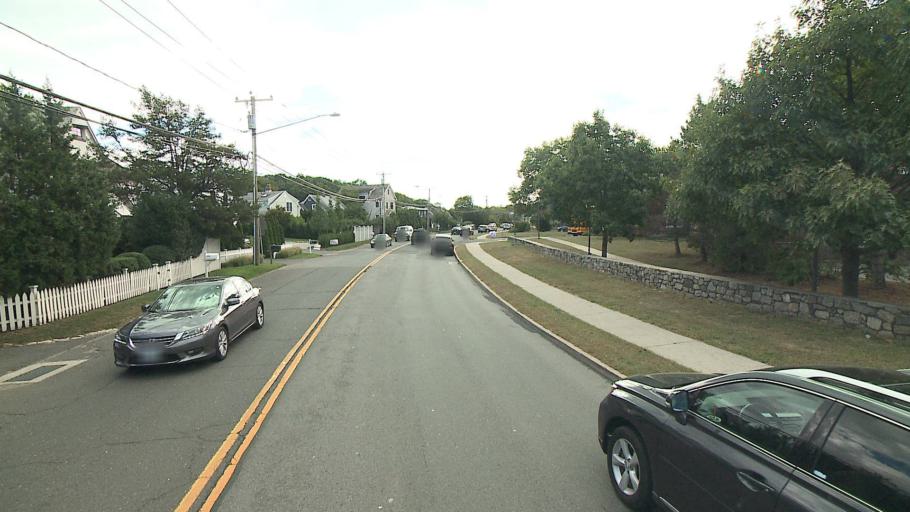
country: US
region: Connecticut
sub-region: Fairfield County
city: Westport
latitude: 41.1346
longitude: -73.3650
